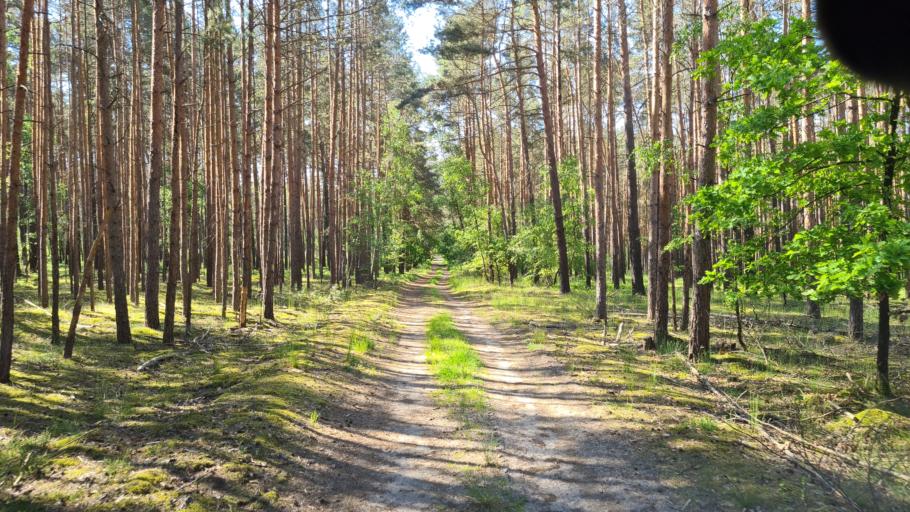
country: DE
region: Brandenburg
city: Ruckersdorf
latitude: 51.6064
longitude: 13.6193
